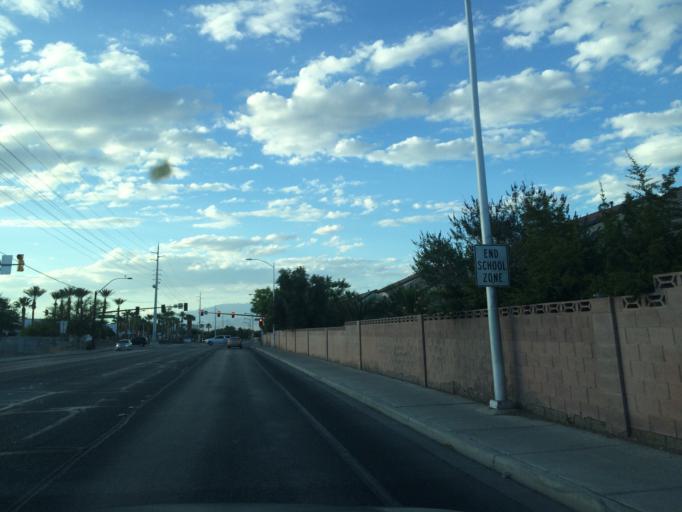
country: US
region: Nevada
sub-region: Clark County
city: Spring Valley
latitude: 36.2023
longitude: -115.2514
